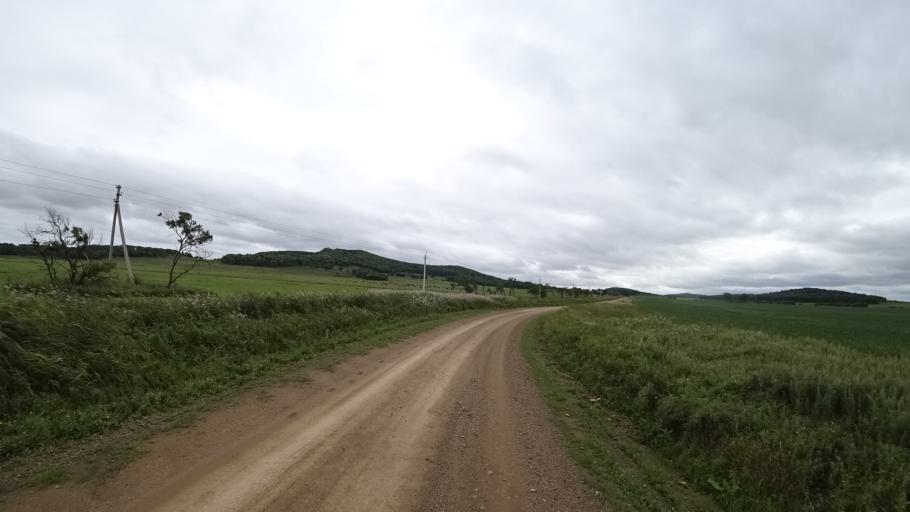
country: RU
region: Primorskiy
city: Chernigovka
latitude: 44.4781
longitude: 132.5784
